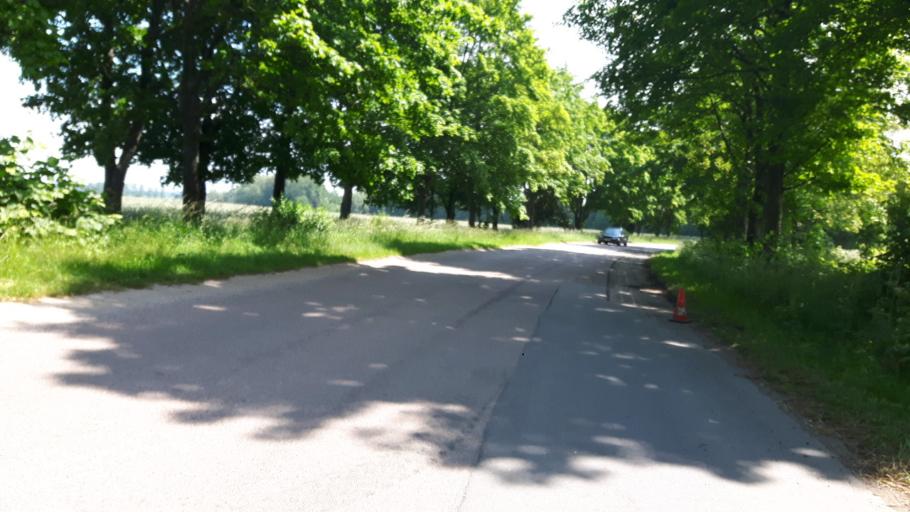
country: PL
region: Pomeranian Voivodeship
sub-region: Powiat wejherowski
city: Choczewo
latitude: 54.7455
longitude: 17.8070
